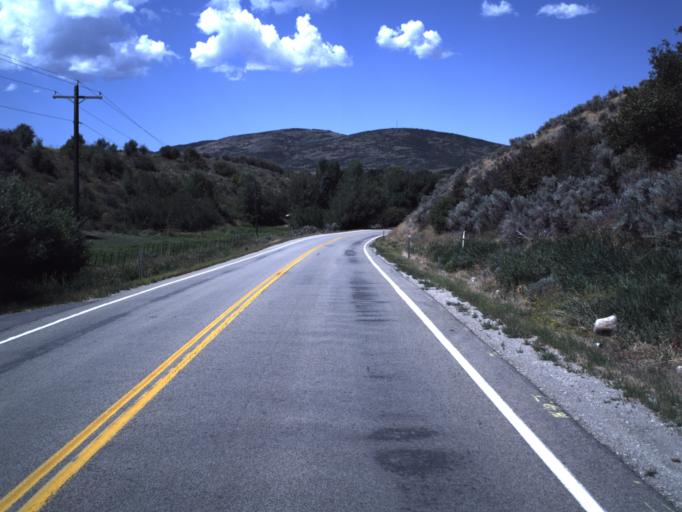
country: US
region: Utah
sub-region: Summit County
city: Oakley
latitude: 40.7236
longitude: -111.3213
